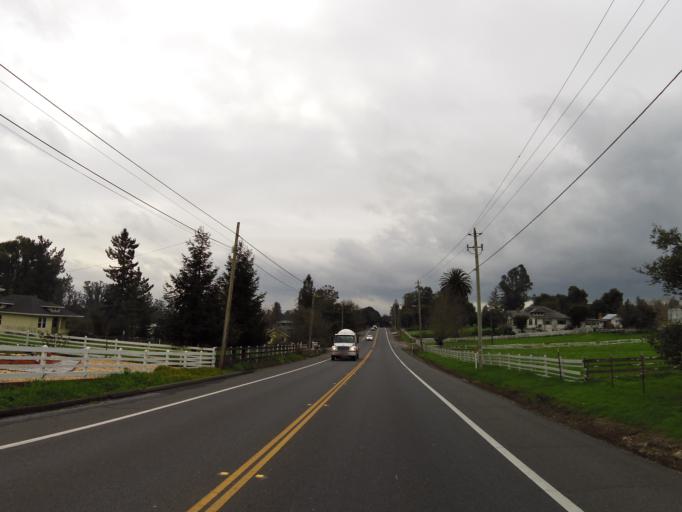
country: US
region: California
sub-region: Sonoma County
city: Penngrove
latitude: 38.3056
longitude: -122.6665
